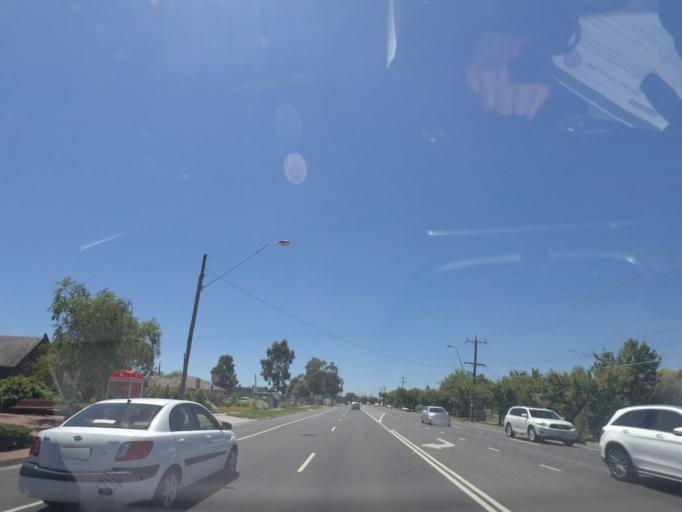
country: AU
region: Victoria
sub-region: Whittlesea
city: Epping
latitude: -37.6470
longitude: 145.0261
